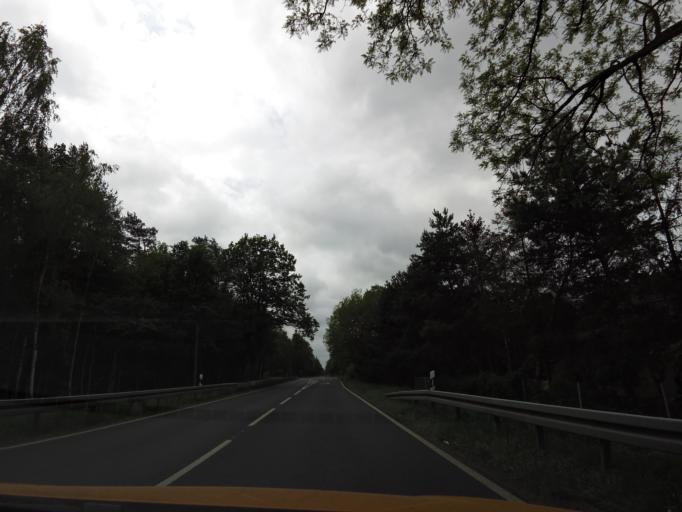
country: DE
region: Brandenburg
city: Beelitz
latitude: 52.1871
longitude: 12.9477
